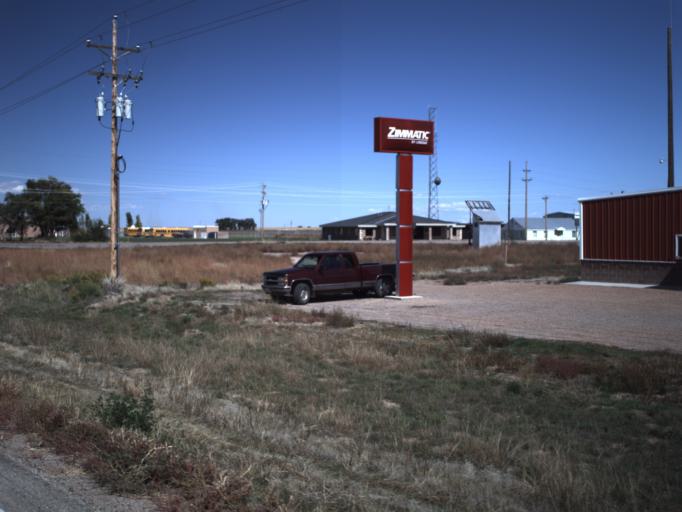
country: US
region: Utah
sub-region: Washington County
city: Enterprise
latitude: 37.7082
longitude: -113.6563
